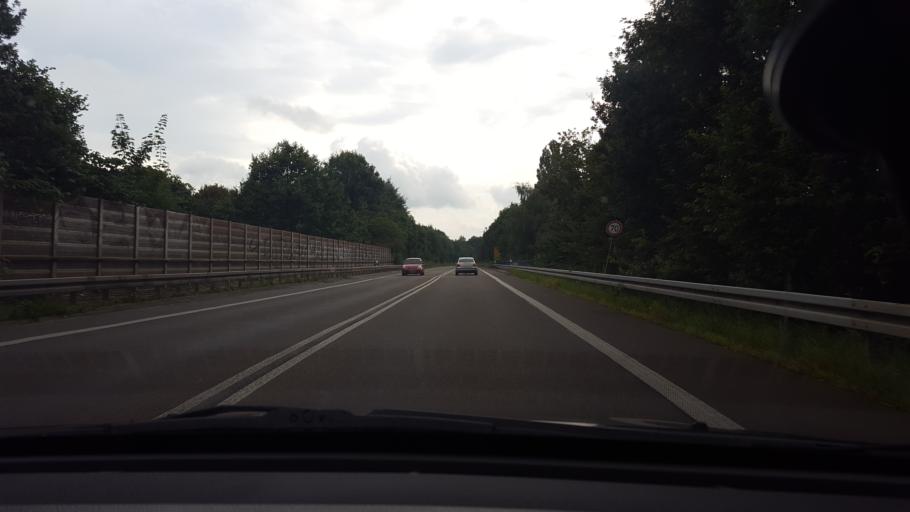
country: DE
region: North Rhine-Westphalia
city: Herten
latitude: 51.6099
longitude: 7.1377
